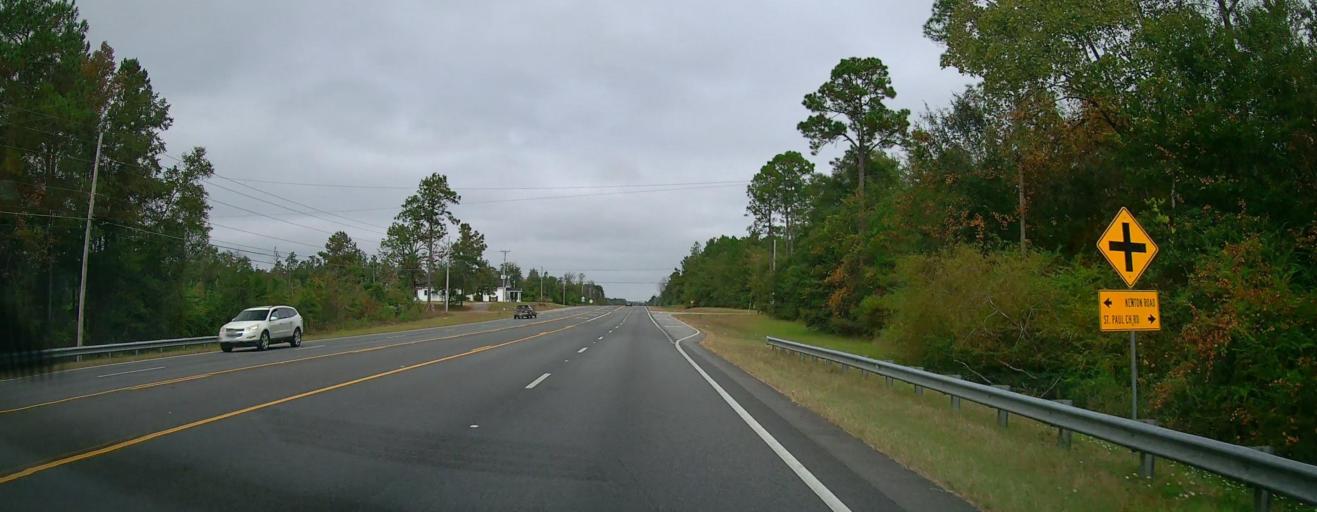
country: US
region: Georgia
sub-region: Thomas County
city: Thomasville
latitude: 30.9230
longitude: -83.9139
